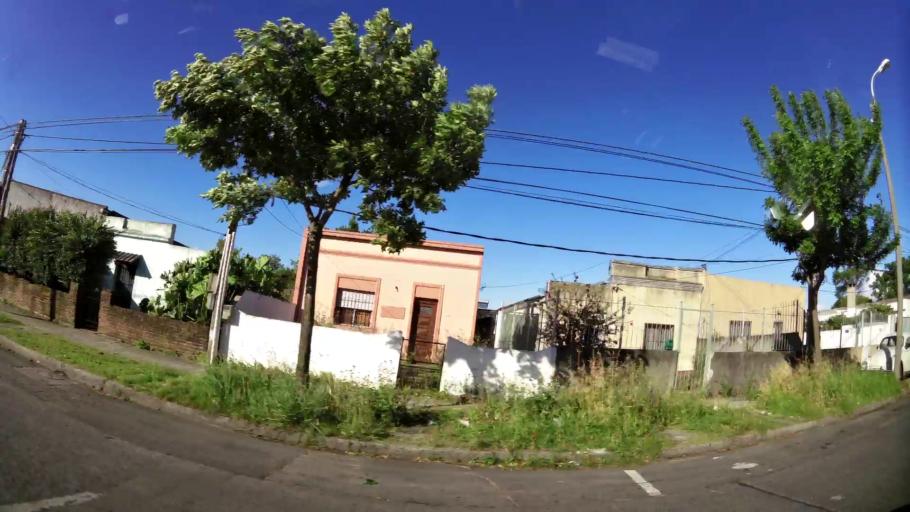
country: UY
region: Montevideo
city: Montevideo
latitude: -34.8546
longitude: -56.2346
